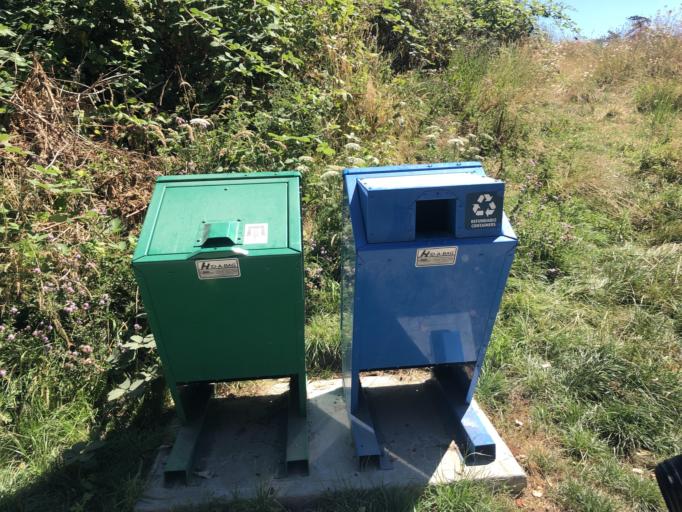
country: CA
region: British Columbia
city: Metchosin
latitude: 48.3855
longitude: -123.5084
